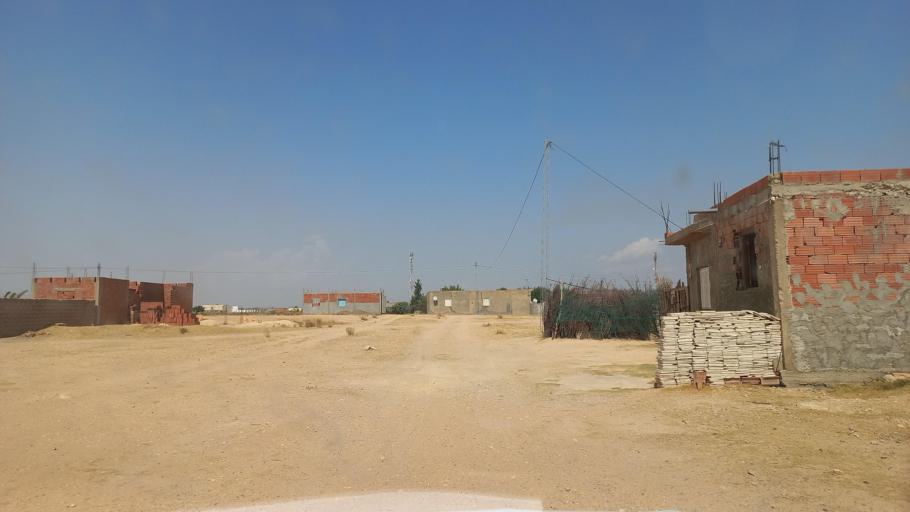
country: TN
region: Al Qasrayn
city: Kasserine
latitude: 35.2500
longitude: 9.0220
